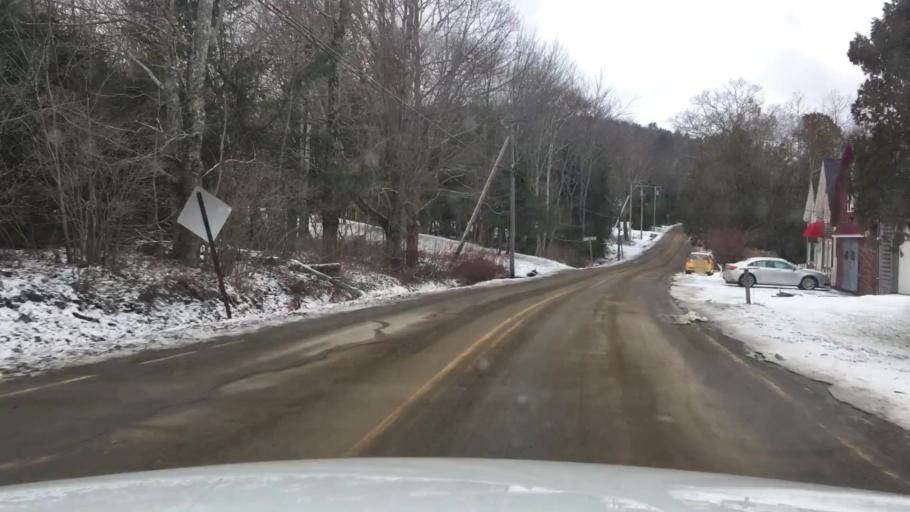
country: US
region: Maine
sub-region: Waldo County
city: Lincolnville
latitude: 44.2818
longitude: -69.0108
